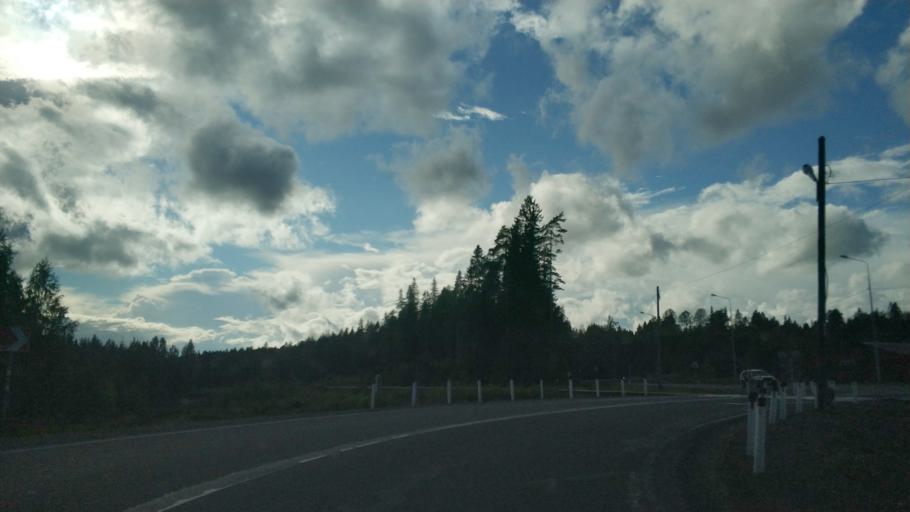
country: RU
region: Republic of Karelia
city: Lakhdenpokh'ya
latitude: 61.5132
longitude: 30.1120
